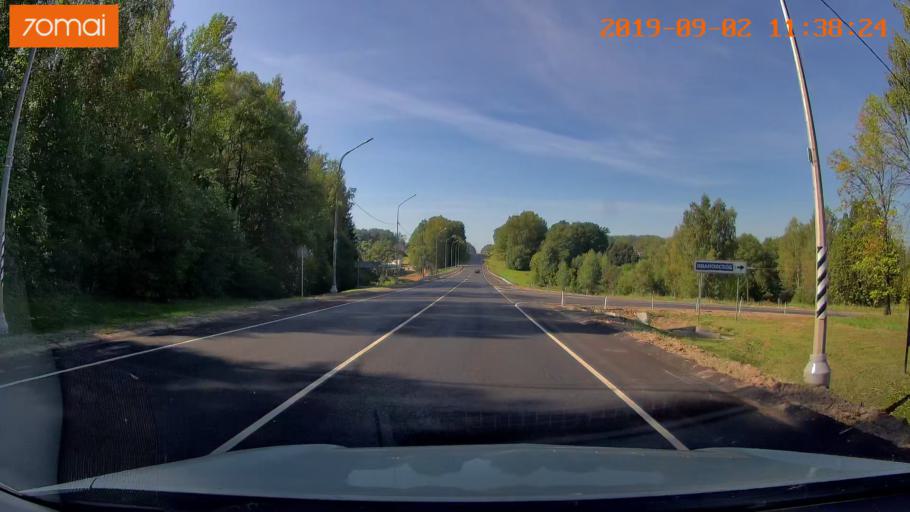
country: RU
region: Smolensk
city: Oster
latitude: 53.9135
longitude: 32.7414
